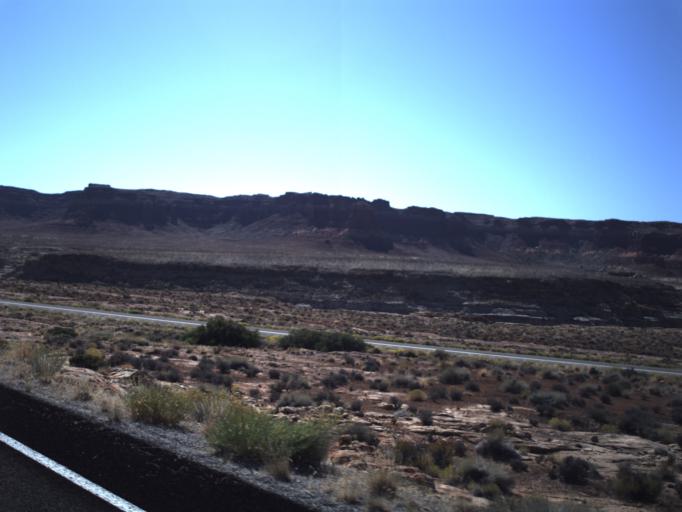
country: US
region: Utah
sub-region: San Juan County
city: Blanding
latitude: 37.8955
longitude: -110.3782
